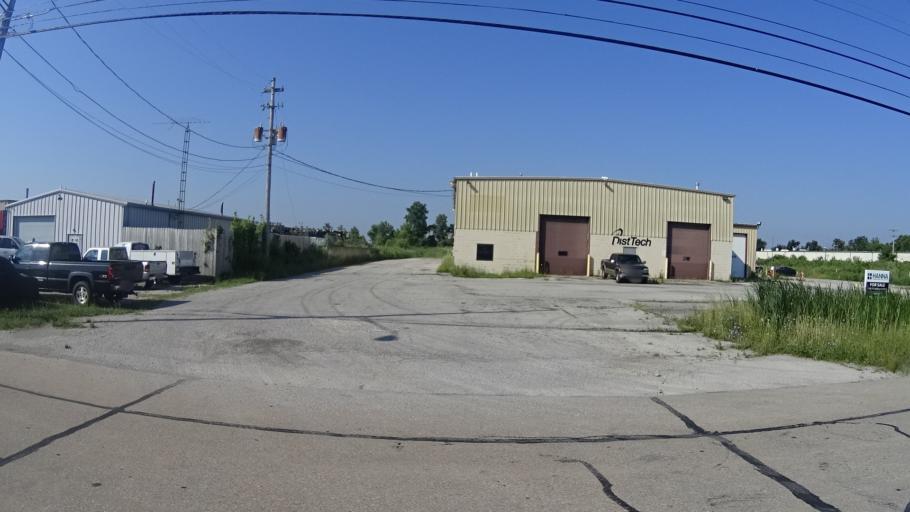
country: US
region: Ohio
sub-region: Erie County
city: Huron
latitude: 41.3997
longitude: -82.5836
